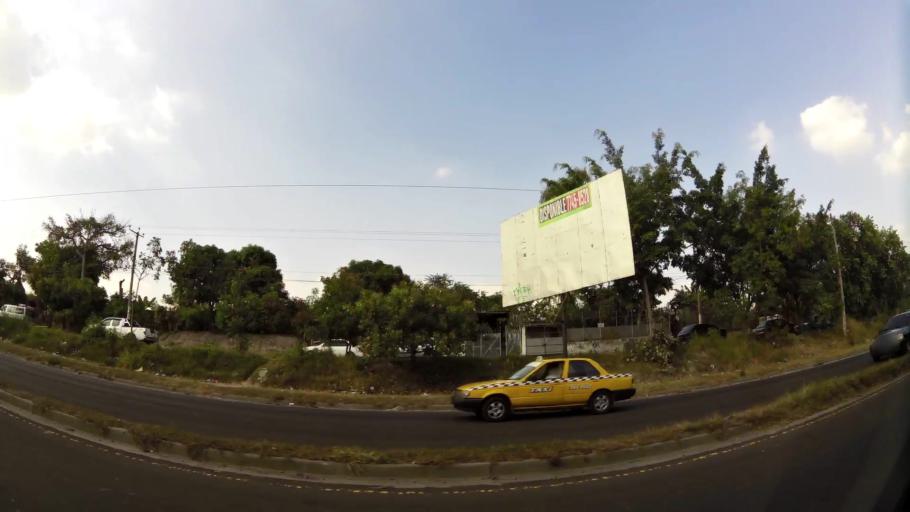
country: SV
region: San Salvador
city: Soyapango
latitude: 13.7177
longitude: -89.1358
